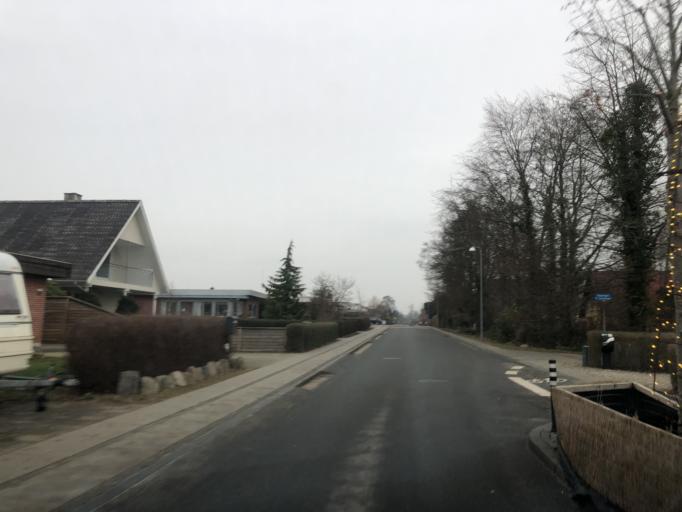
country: DK
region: South Denmark
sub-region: Faaborg-Midtfyn Kommune
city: Arslev
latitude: 55.3050
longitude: 10.4789
